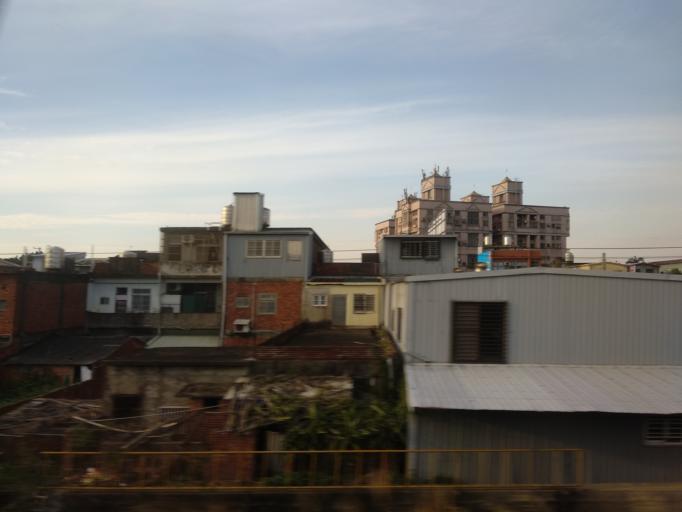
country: TW
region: Taiwan
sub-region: Hsinchu
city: Zhubei
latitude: 24.8893
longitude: 121.0217
